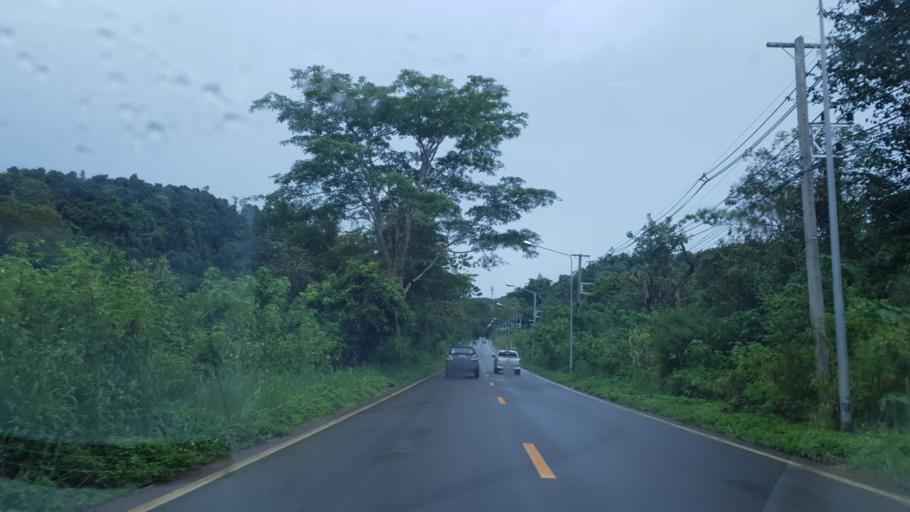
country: TH
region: Mae Hong Son
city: Ban Huai I Huak
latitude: 18.1611
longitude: 98.0673
